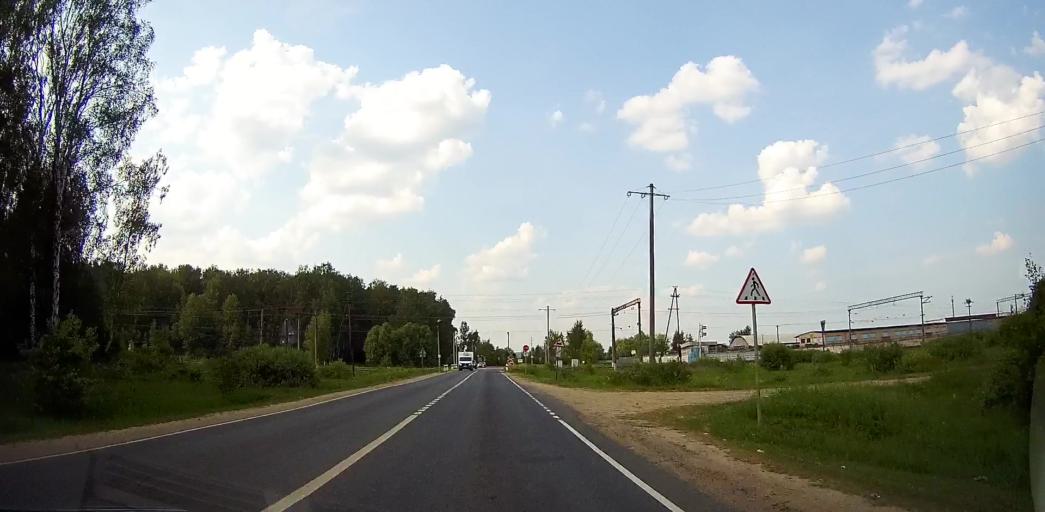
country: RU
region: Moskovskaya
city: Malino
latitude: 55.0548
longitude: 38.1423
